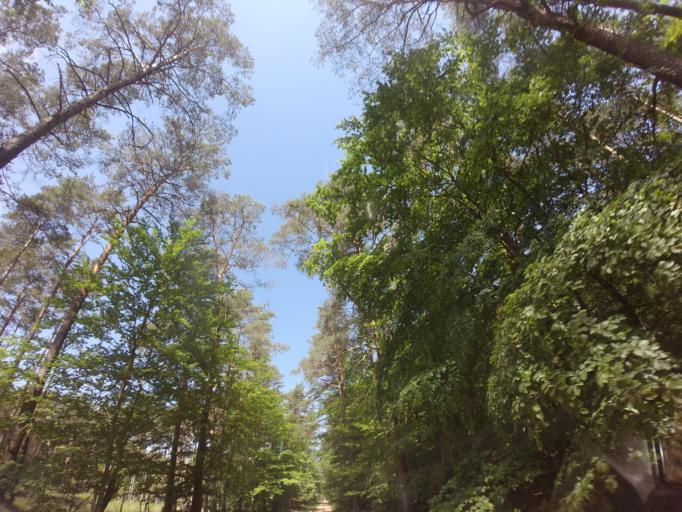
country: PL
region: West Pomeranian Voivodeship
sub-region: Powiat choszczenski
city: Drawno
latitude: 53.1503
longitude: 15.8105
